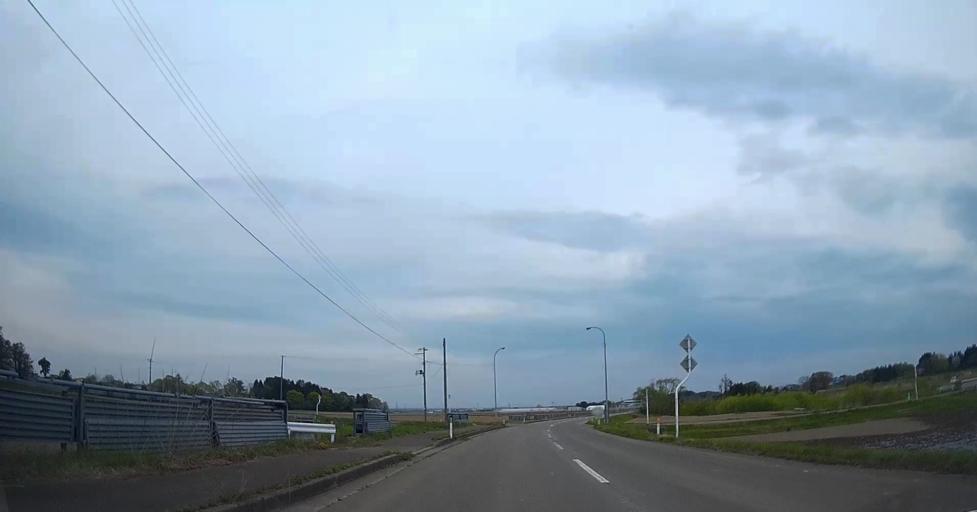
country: JP
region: Aomori
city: Goshogawara
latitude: 40.8986
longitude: 140.4853
